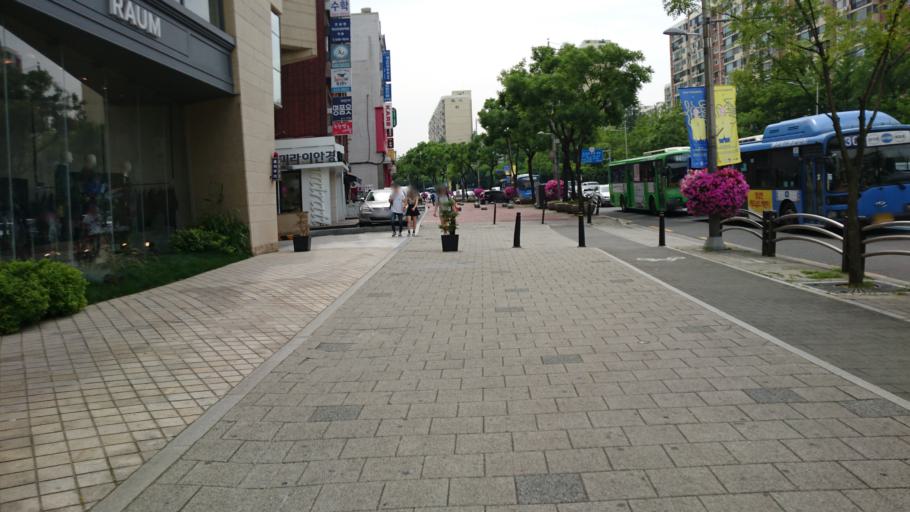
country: KR
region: Seoul
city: Seoul
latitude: 37.5289
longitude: 127.0333
